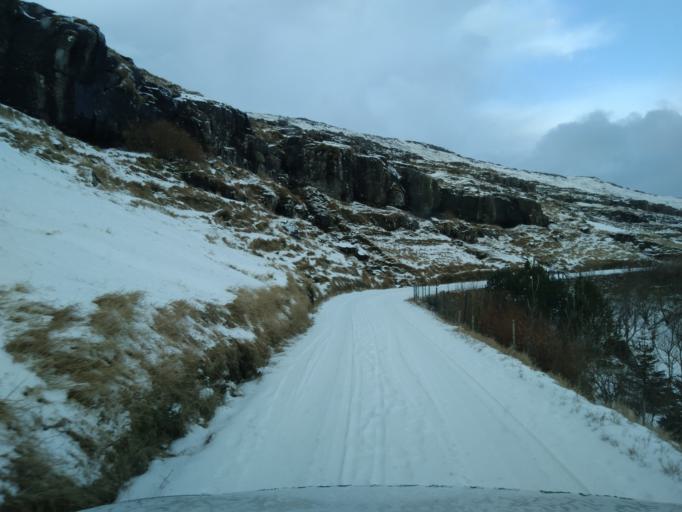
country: FO
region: Eysturoy
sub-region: Eidi
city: Eidi
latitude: 62.3033
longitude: -7.0909
